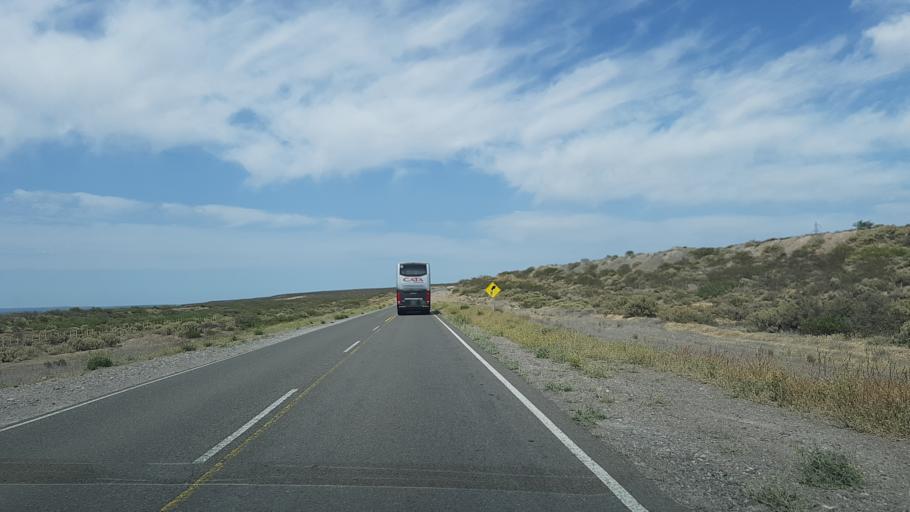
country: AR
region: Neuquen
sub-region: Departamento de Picun Leufu
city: Picun Leufu
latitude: -39.6556
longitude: -69.4128
